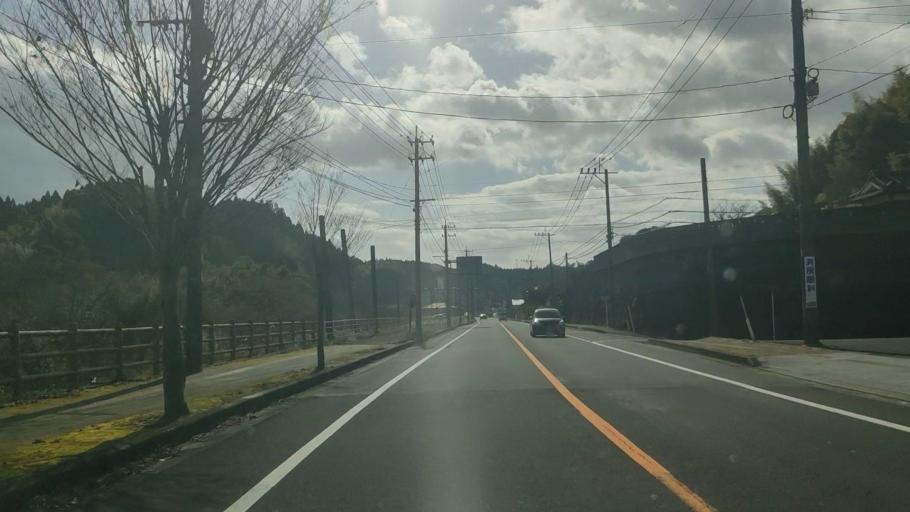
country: JP
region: Kagoshima
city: Okuchi-shinohara
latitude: 31.9455
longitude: 130.7111
